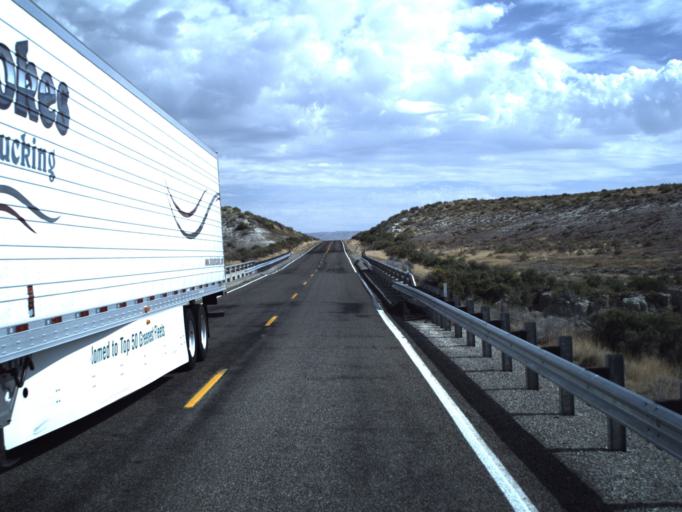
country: US
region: Utah
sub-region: Tooele County
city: Wendover
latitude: 41.4071
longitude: -113.9365
